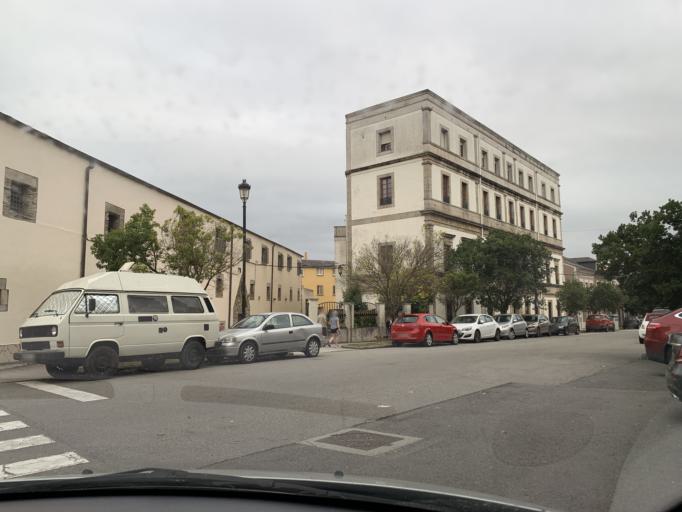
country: ES
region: Galicia
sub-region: Provincia de Lugo
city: Ribadeo
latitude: 43.5351
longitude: -7.0403
